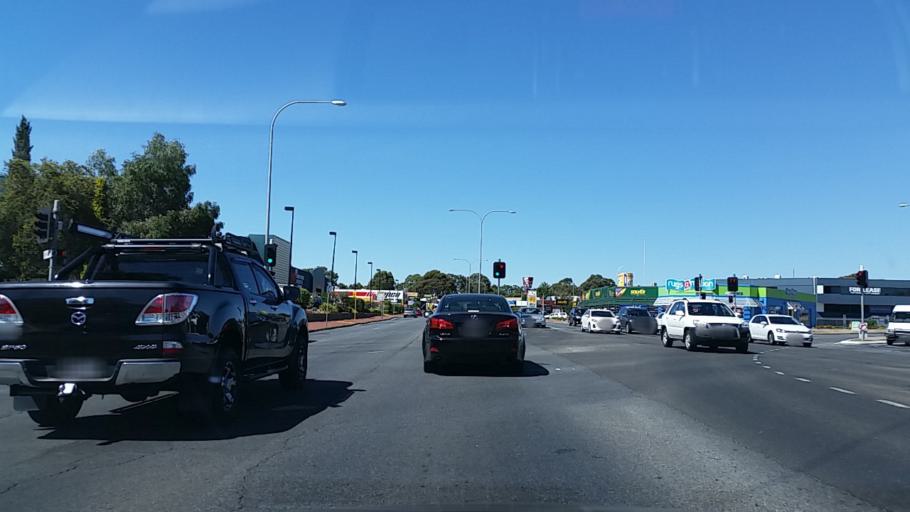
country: AU
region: South Australia
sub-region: Tea Tree Gully
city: Modbury
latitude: -34.8339
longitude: 138.6827
